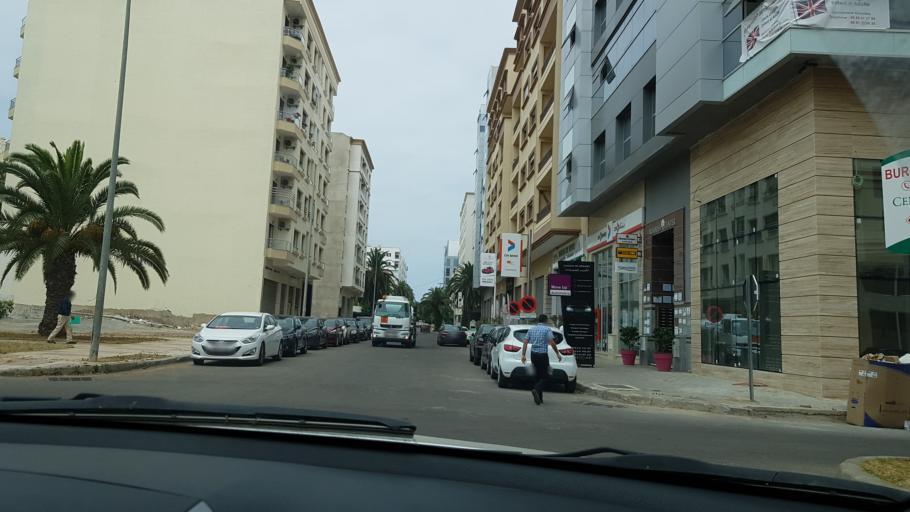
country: MA
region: Grand Casablanca
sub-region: Mohammedia
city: Mohammedia
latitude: 33.7041
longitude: -7.3972
